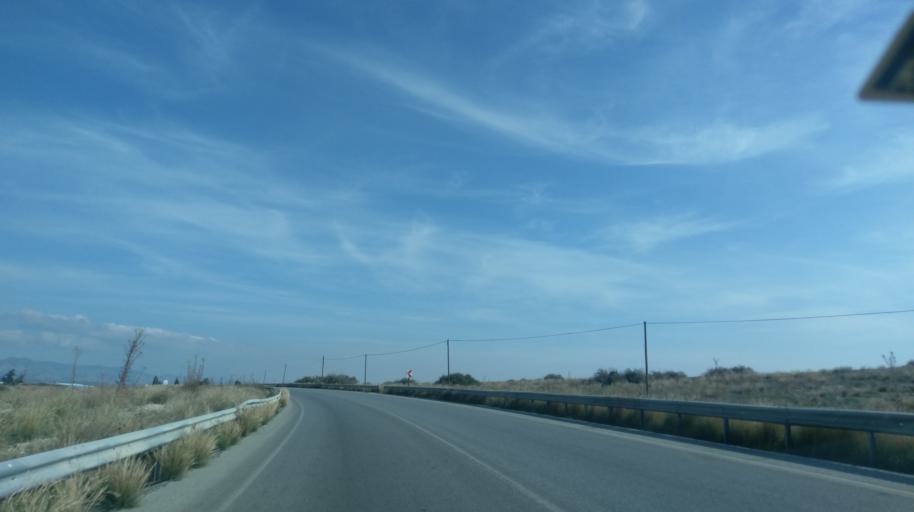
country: CY
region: Ammochostos
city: Lefkonoiko
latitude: 35.2520
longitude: 33.6293
